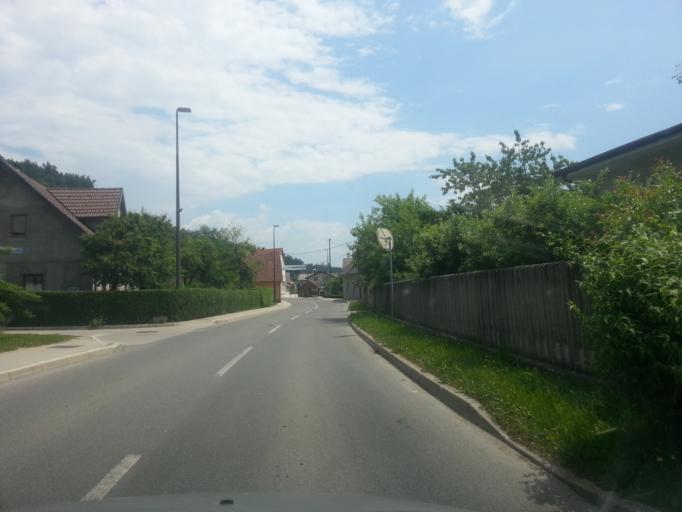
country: SI
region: Horjul
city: Horjul
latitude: 46.0222
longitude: 14.2957
